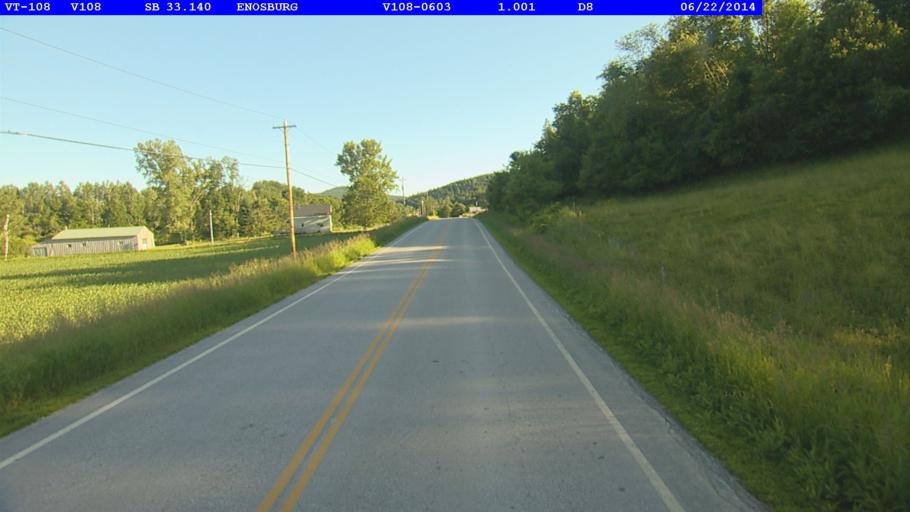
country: US
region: Vermont
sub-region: Franklin County
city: Enosburg Falls
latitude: 44.8523
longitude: -72.8042
